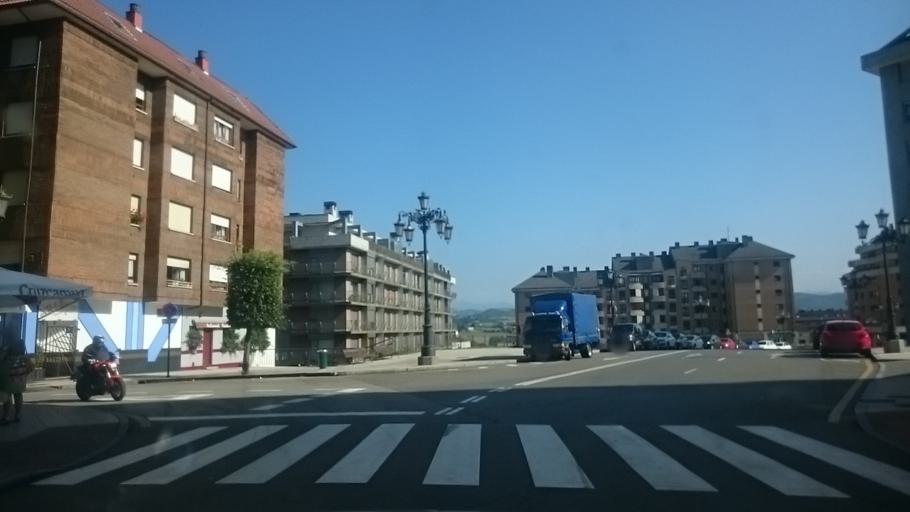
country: ES
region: Asturias
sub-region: Province of Asturias
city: Oviedo
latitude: 43.3548
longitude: -5.8611
